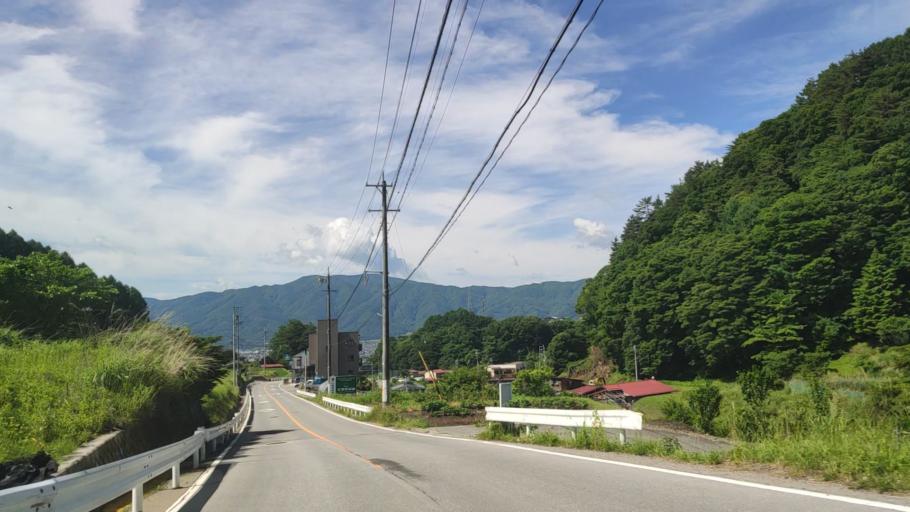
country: JP
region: Nagano
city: Suwa
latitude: 36.0529
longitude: 138.1284
